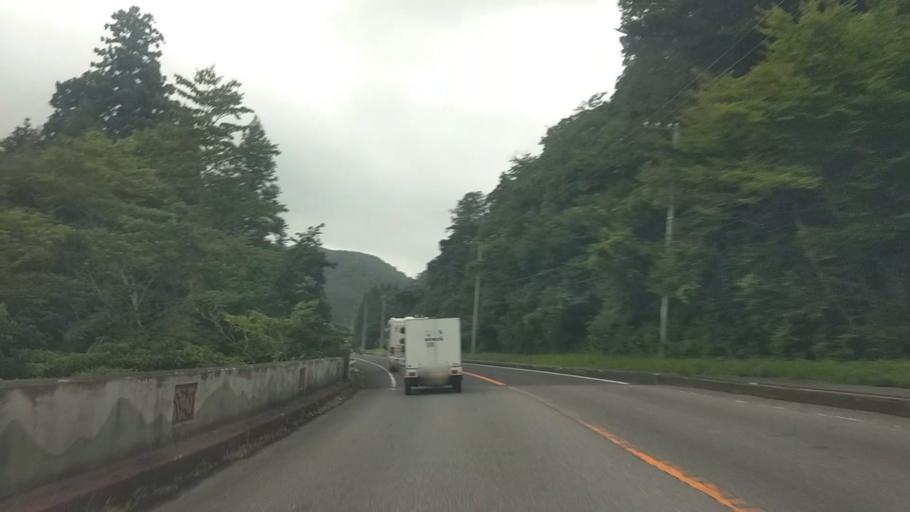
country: JP
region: Chiba
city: Kawaguchi
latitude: 35.1859
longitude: 140.0605
